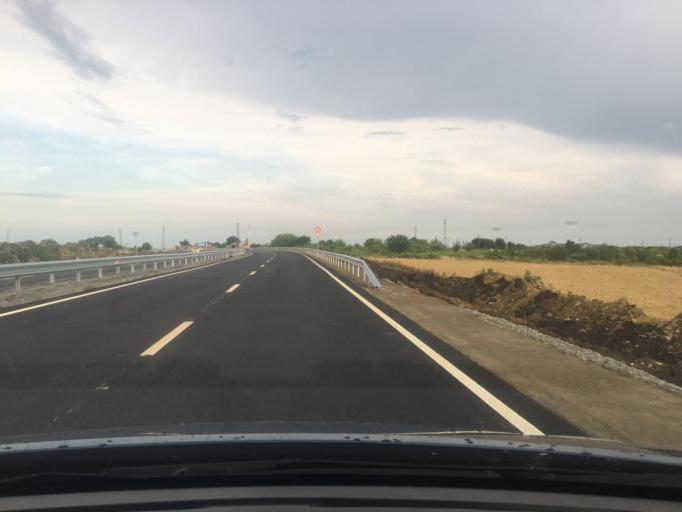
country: BG
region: Burgas
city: Aheloy
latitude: 42.6531
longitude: 27.6628
